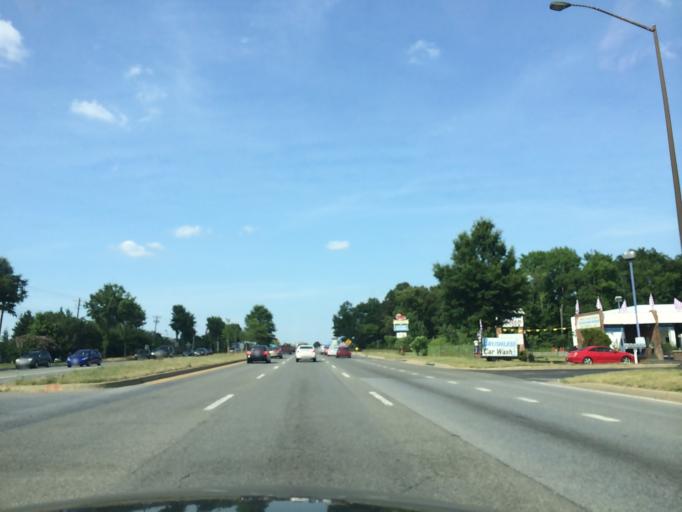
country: US
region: Maryland
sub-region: Charles County
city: Waldorf
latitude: 38.6446
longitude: -76.8915
